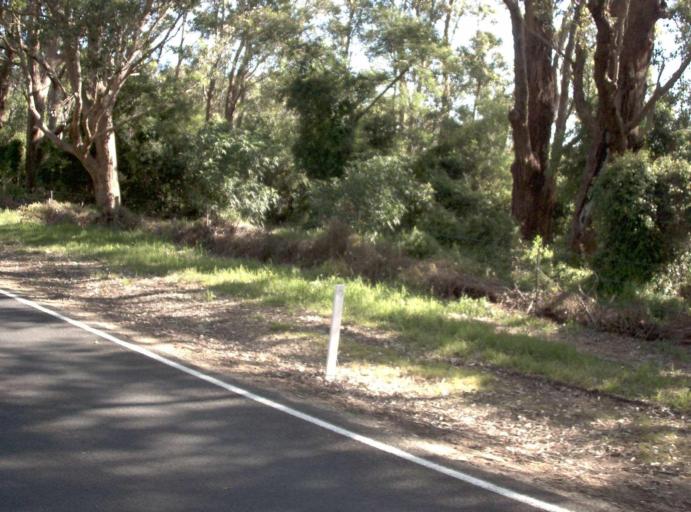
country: AU
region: Victoria
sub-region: East Gippsland
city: Lakes Entrance
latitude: -37.7495
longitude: 148.5183
